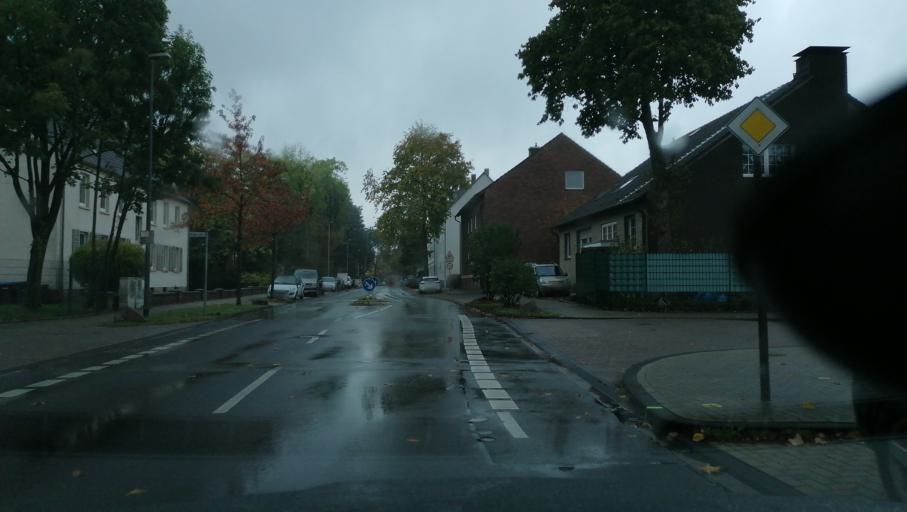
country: DE
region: North Rhine-Westphalia
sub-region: Regierungsbezirk Munster
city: Gelsenkirchen
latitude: 51.5423
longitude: 7.1409
